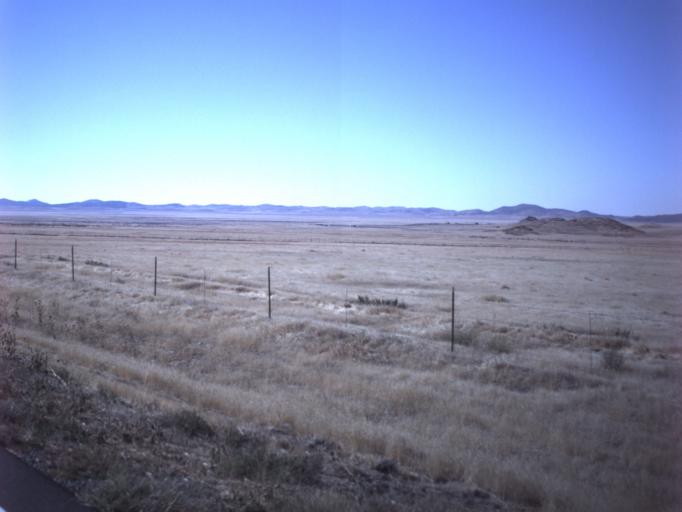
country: US
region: Utah
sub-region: Tooele County
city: Grantsville
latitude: 40.3929
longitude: -112.7475
